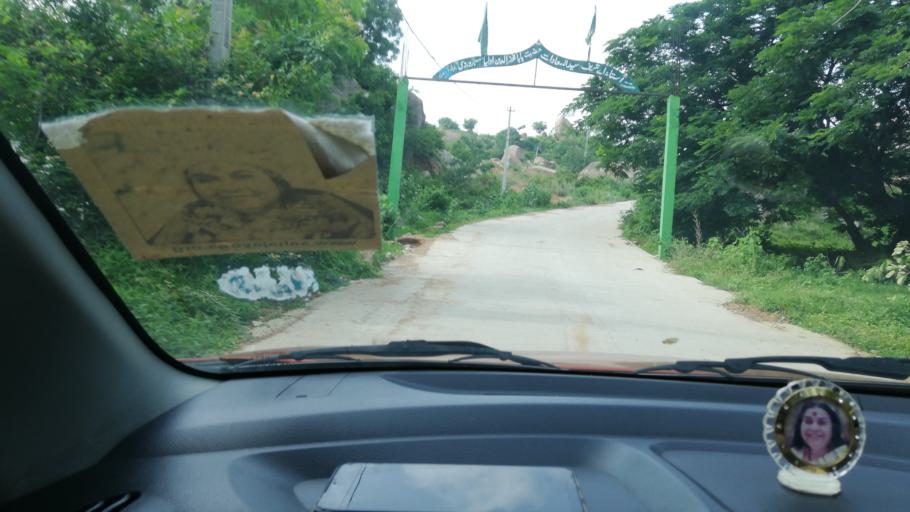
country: IN
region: Telangana
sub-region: Rangareddi
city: Kukatpalli
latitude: 17.4129
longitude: 78.3661
